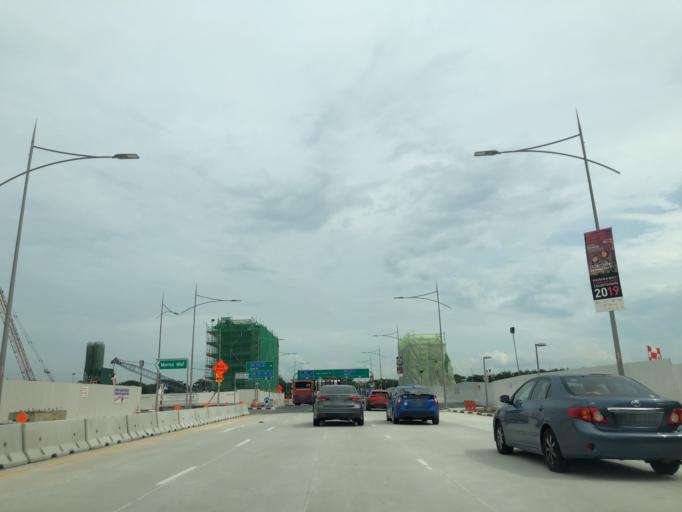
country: SG
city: Singapore
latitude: 1.2752
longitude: 103.8627
